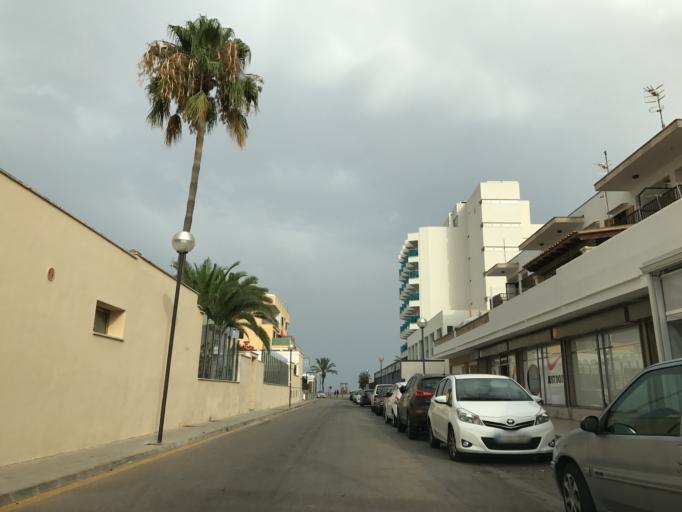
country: ES
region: Balearic Islands
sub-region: Illes Balears
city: Son Servera
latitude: 39.5976
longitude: 3.3828
